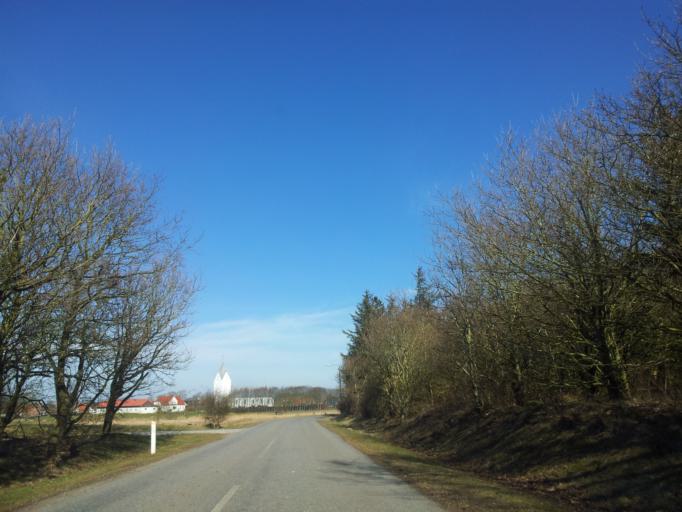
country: DK
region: South Denmark
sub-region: Tonder Kommune
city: Sherrebek
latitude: 55.1905
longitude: 8.7222
